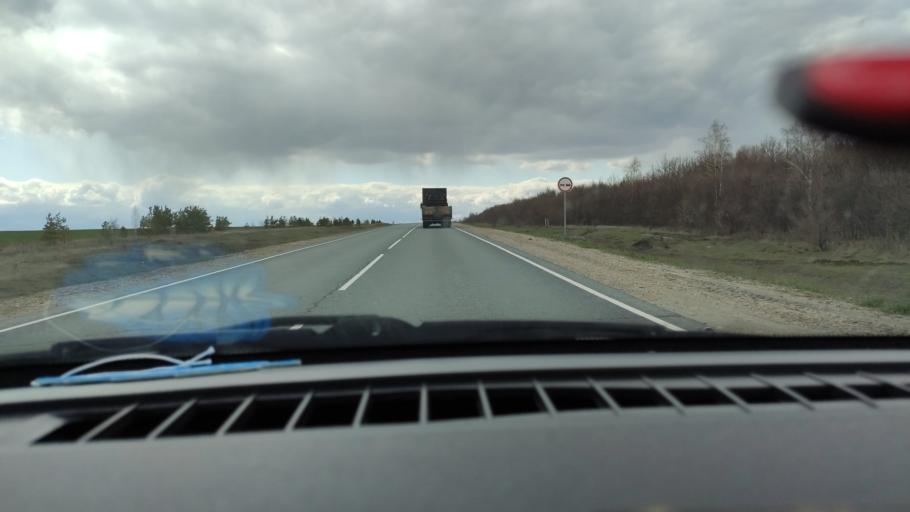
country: RU
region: Saratov
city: Alekseyevka
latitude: 52.2350
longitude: 47.9044
